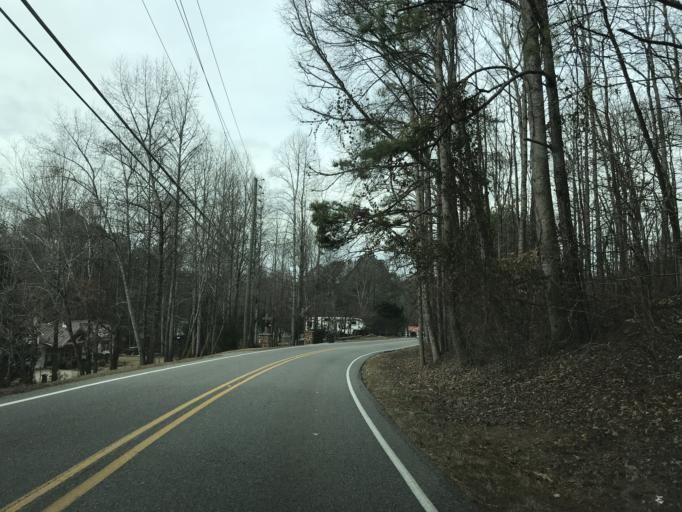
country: US
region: Georgia
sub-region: Fulton County
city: Milton
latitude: 34.2003
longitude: -84.3842
